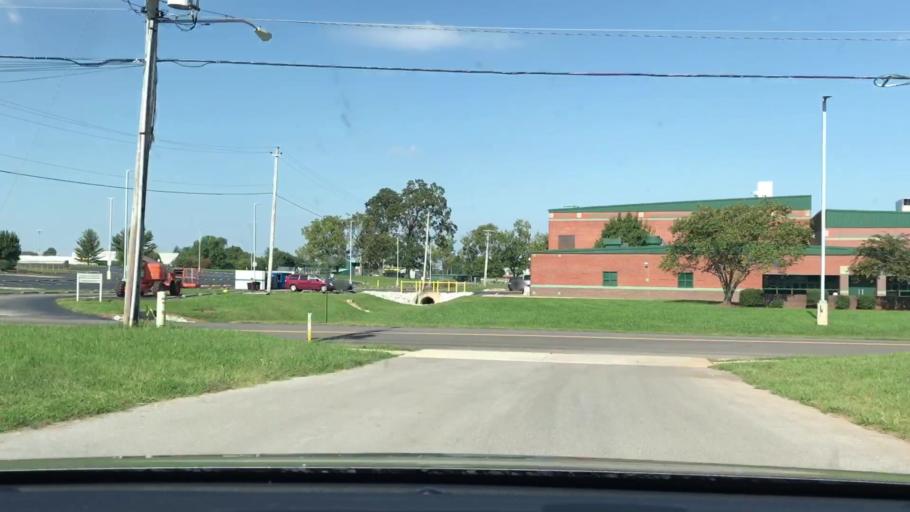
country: US
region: Kentucky
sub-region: Warren County
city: Plano
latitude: 36.9252
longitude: -86.4133
